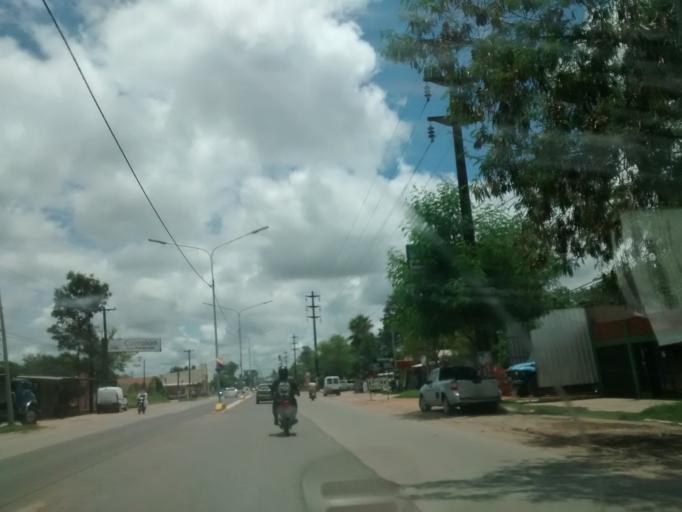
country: AR
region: Chaco
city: Resistencia
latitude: -27.4290
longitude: -58.9792
